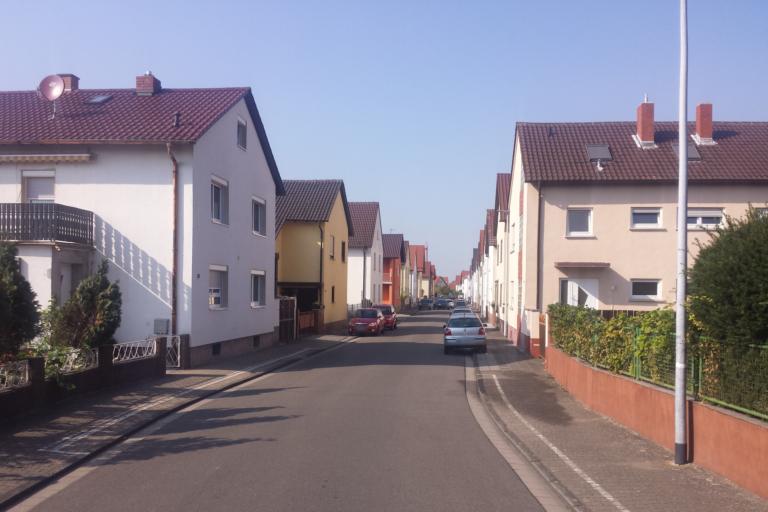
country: DE
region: Rheinland-Pfalz
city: Waldsee
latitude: 49.3927
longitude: 8.4350
